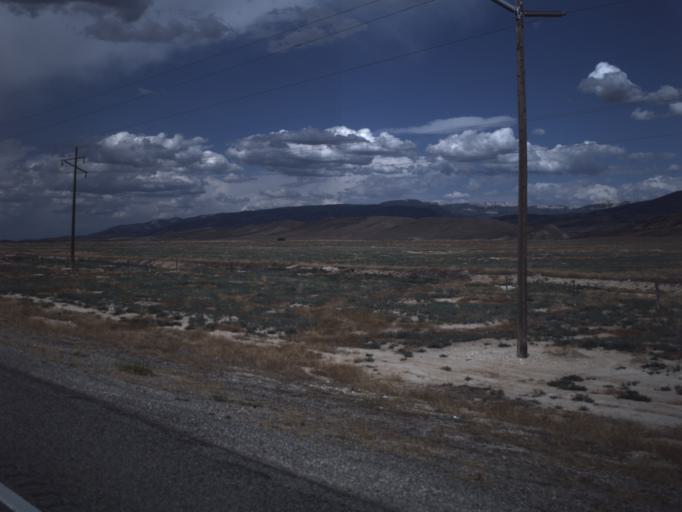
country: US
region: Utah
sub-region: Sevier County
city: Salina
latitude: 39.0226
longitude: -111.8323
